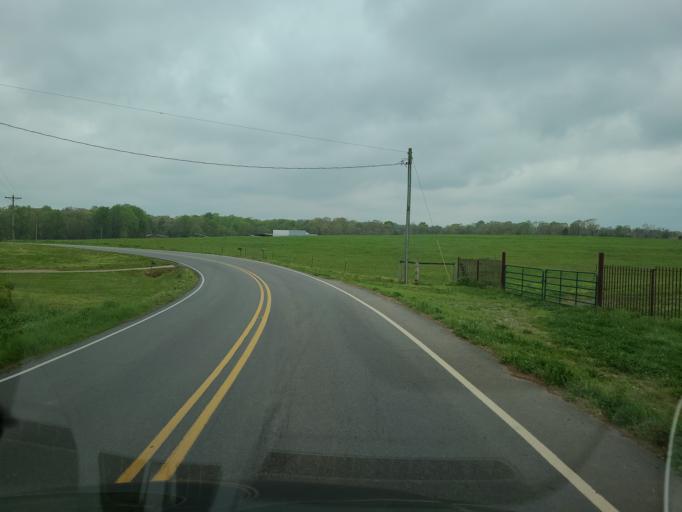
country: US
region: North Carolina
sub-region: Gaston County
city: Cherryville
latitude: 35.4558
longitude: -81.3449
